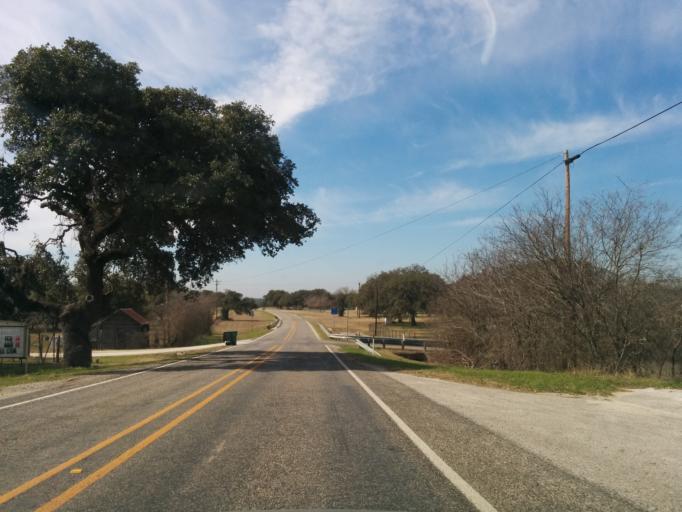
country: US
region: Texas
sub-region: Blanco County
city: Blanco
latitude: 29.9685
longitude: -98.5240
